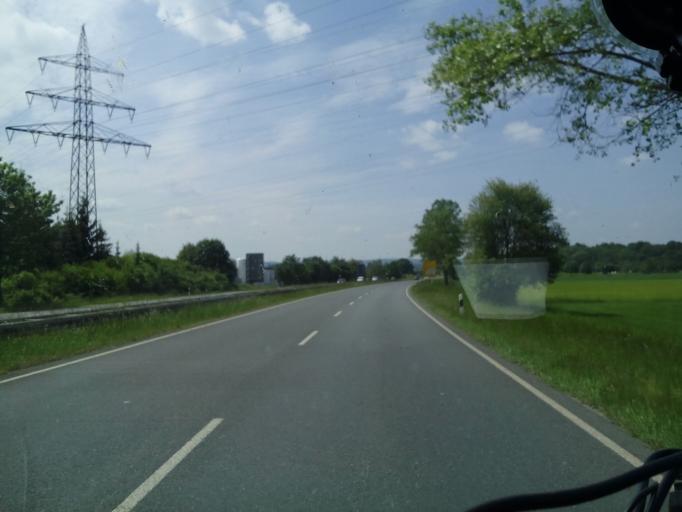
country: DE
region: Bavaria
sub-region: Upper Franconia
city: Kulmbach
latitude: 50.1067
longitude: 11.4274
